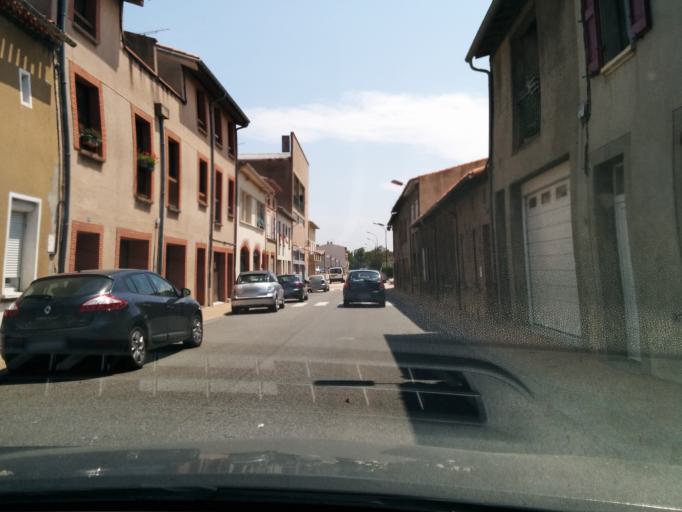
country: FR
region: Midi-Pyrenees
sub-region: Departement de la Haute-Garonne
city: Villefranche-de-Lauragais
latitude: 43.3985
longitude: 1.7160
